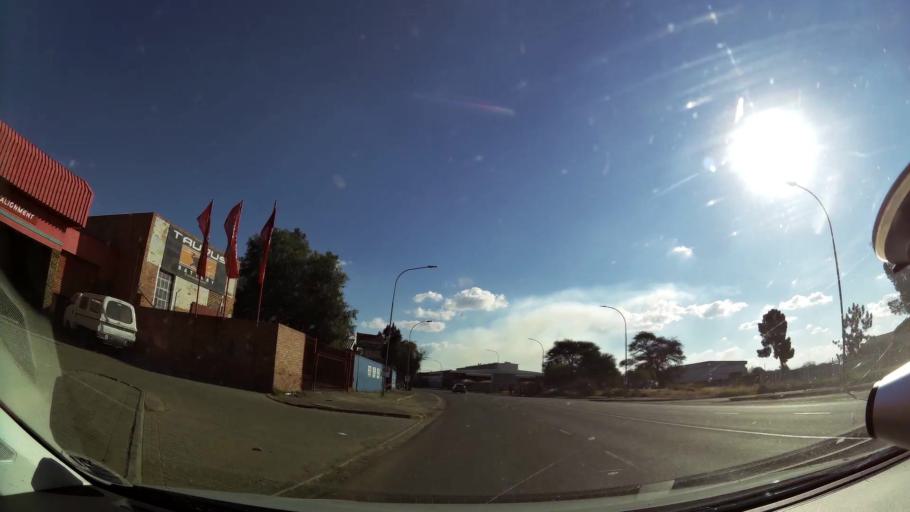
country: ZA
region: Northern Cape
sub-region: Frances Baard District Municipality
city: Kimberley
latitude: -28.7307
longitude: 24.7636
